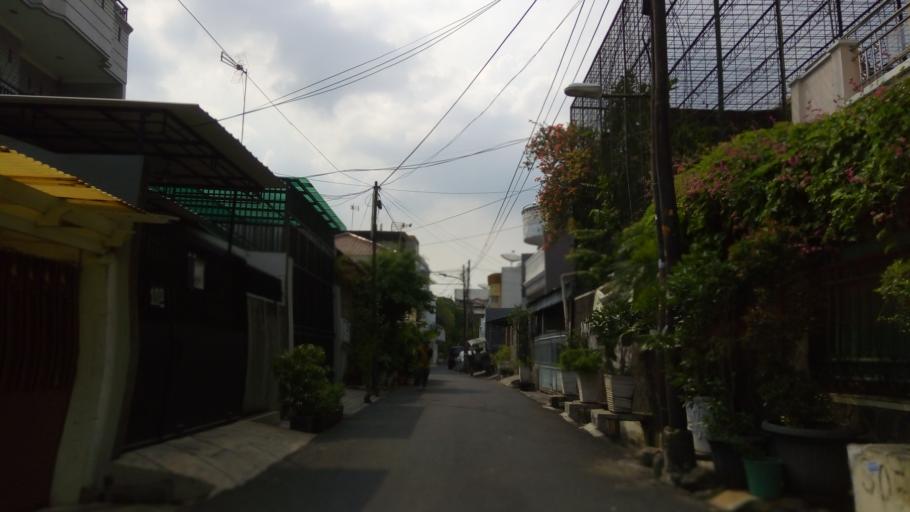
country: ID
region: Jakarta Raya
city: Jakarta
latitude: -6.1555
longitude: 106.8347
